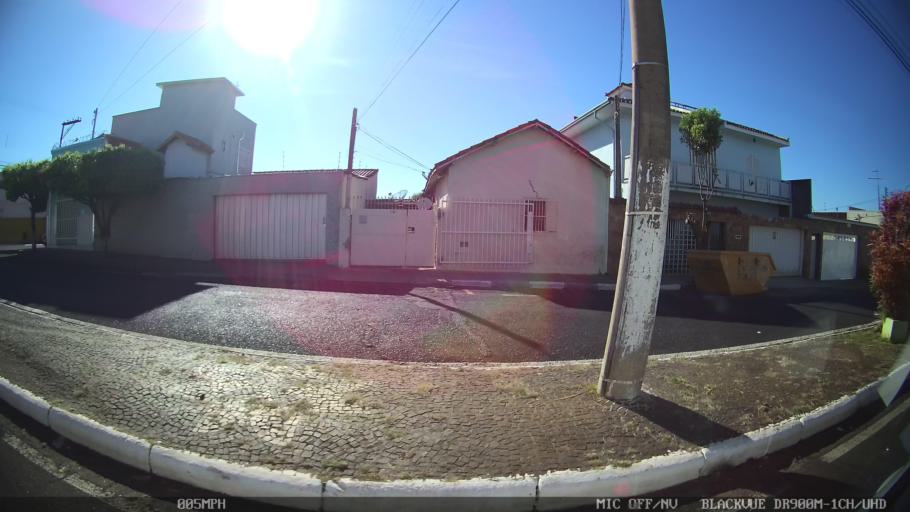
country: BR
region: Sao Paulo
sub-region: Franca
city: Franca
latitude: -20.5406
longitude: -47.4129
